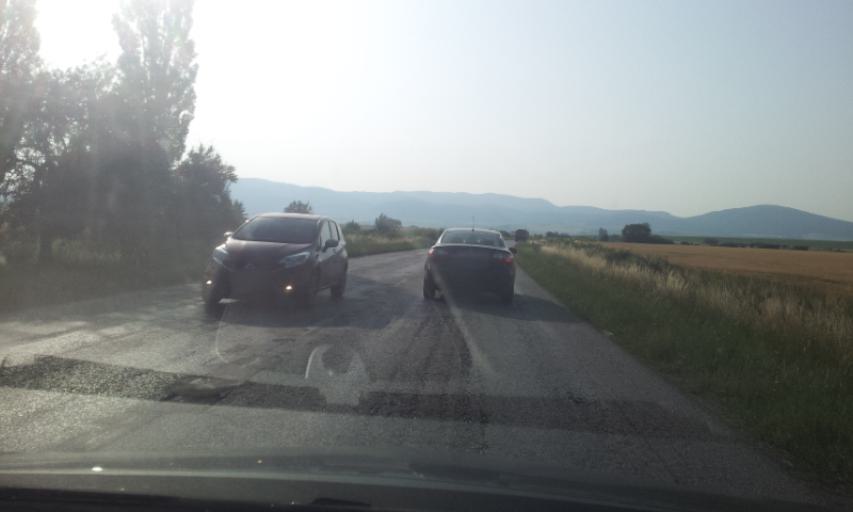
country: SK
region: Kosicky
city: Kosice
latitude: 48.6133
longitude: 21.2784
